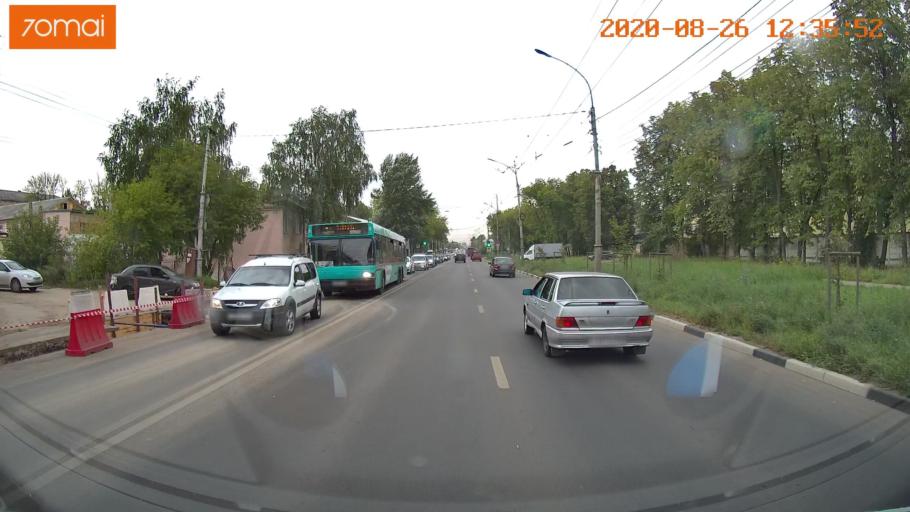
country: RU
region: Rjazan
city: Ryazan'
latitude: 54.5990
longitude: 39.7667
